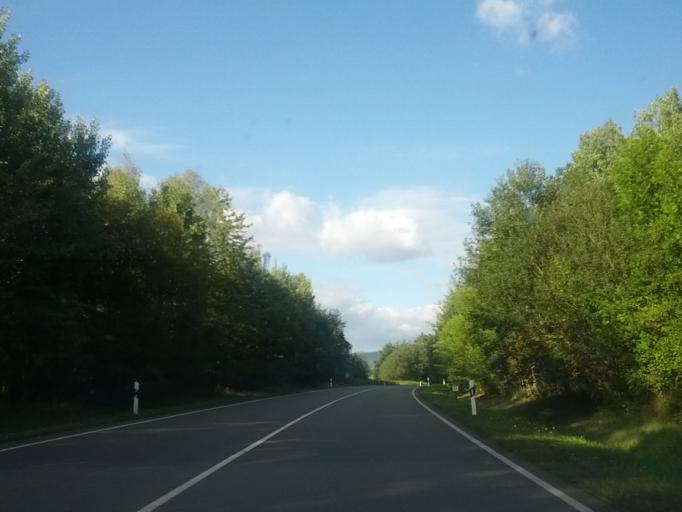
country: DE
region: Thuringia
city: Barchfeld
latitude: 50.7868
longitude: 10.3152
